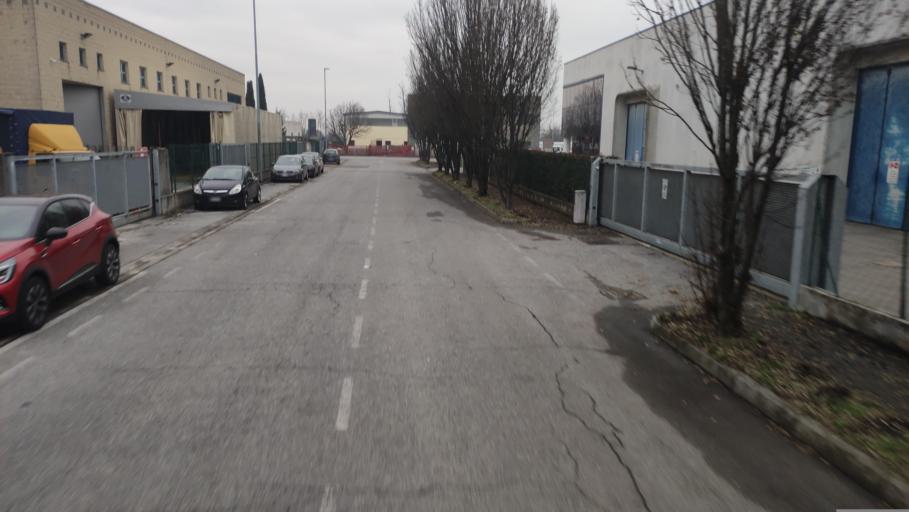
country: IT
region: Lombardy
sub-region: Provincia di Cremona
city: Bagnolo Cremasco
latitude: 45.3652
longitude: 9.6257
